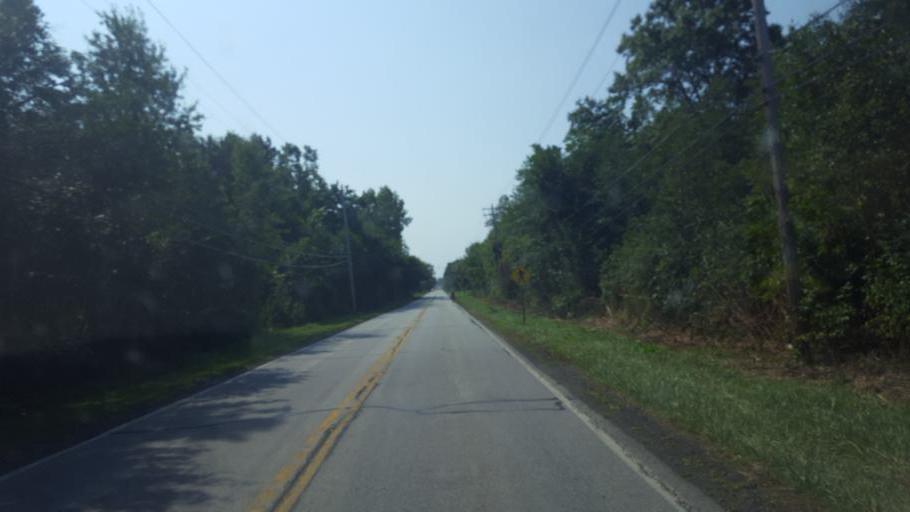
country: US
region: Ohio
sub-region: Lake County
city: Painesville
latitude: 41.7658
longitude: -81.2080
